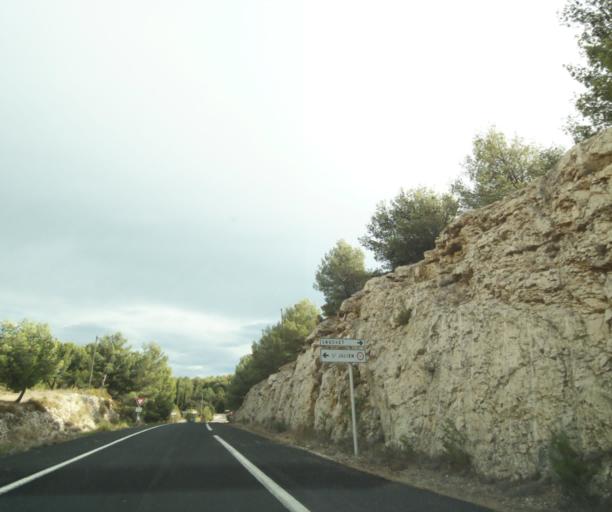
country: FR
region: Provence-Alpes-Cote d'Azur
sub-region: Departement des Bouches-du-Rhone
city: Sausset-les-Pins
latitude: 43.3413
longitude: 5.1038
